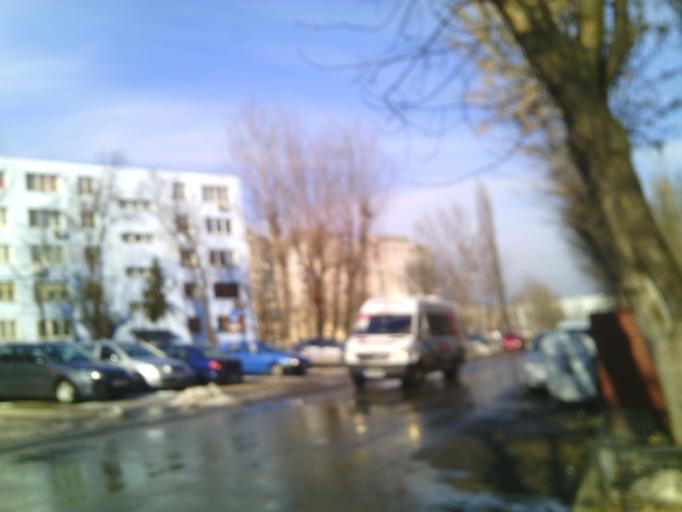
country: RO
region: Bucuresti
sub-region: Municipiul Bucuresti
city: Bucuresti
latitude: 44.3819
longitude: 26.1032
